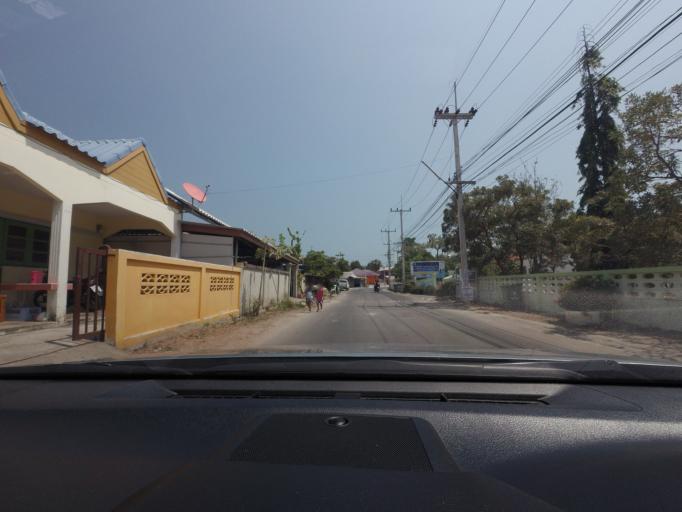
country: TH
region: Phetchaburi
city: Cha-am
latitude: 12.8164
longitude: 99.9892
